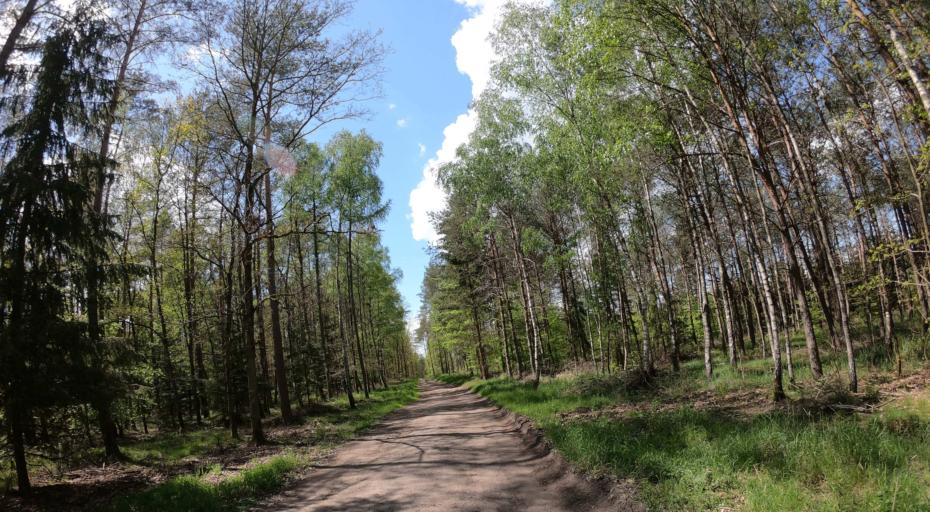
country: PL
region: West Pomeranian Voivodeship
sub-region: Powiat lobeski
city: Lobez
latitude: 53.5971
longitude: 15.6347
